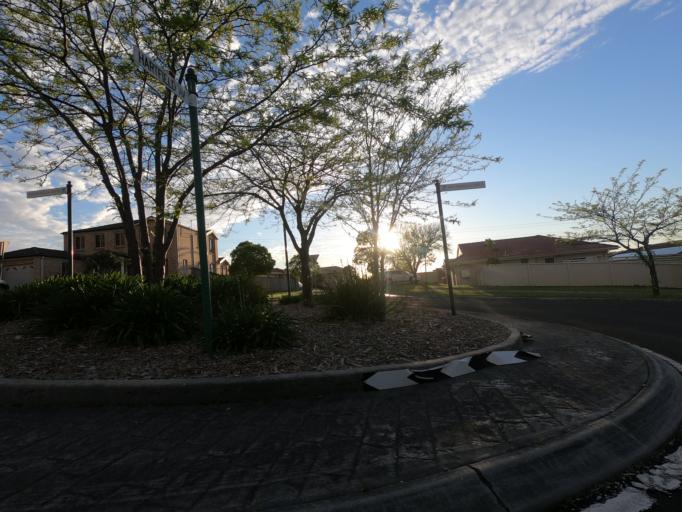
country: AU
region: New South Wales
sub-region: Wollongong
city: Dapto
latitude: -34.4939
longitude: 150.7691
